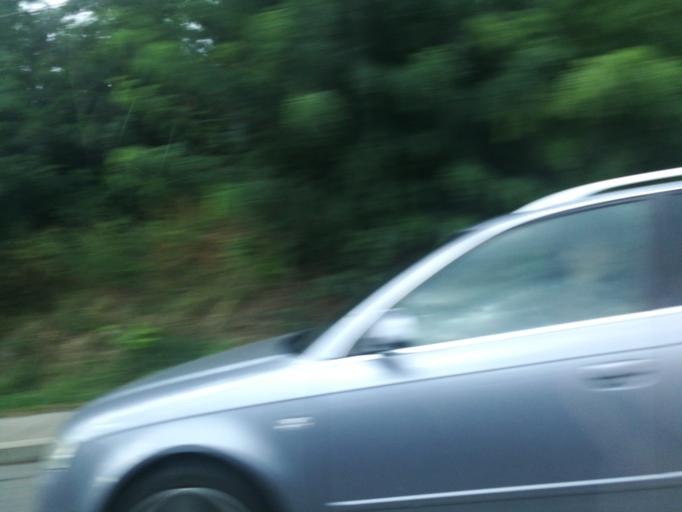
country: RO
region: Mures
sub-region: Comuna Sangeorgiu de Mures
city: Sangeorgiu de Mures
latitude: 46.5743
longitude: 24.6012
